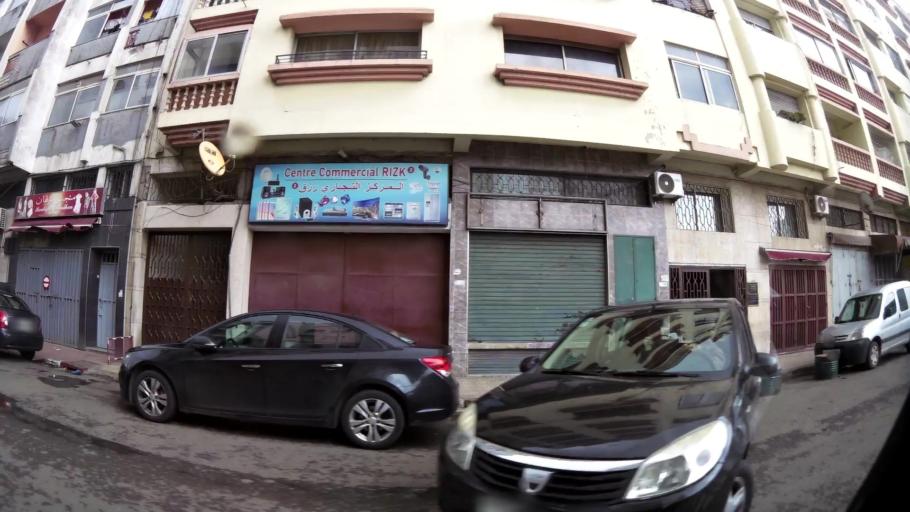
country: MA
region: Grand Casablanca
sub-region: Casablanca
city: Casablanca
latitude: 33.5774
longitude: -7.5985
